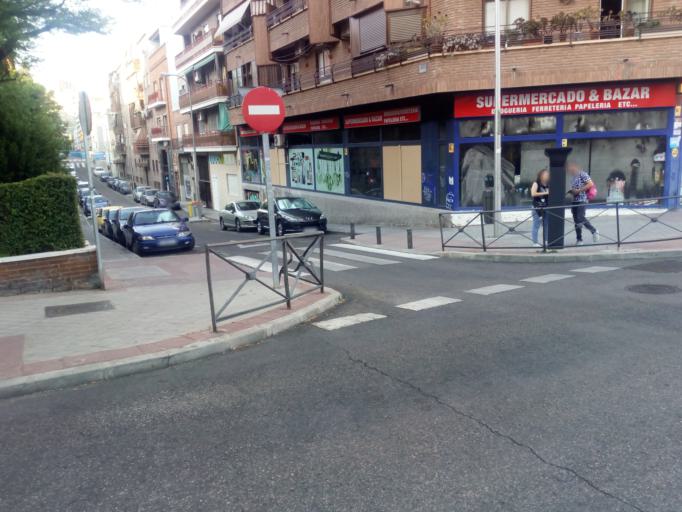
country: ES
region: Madrid
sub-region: Provincia de Madrid
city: Puente de Vallecas
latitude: 40.4029
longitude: -3.6723
